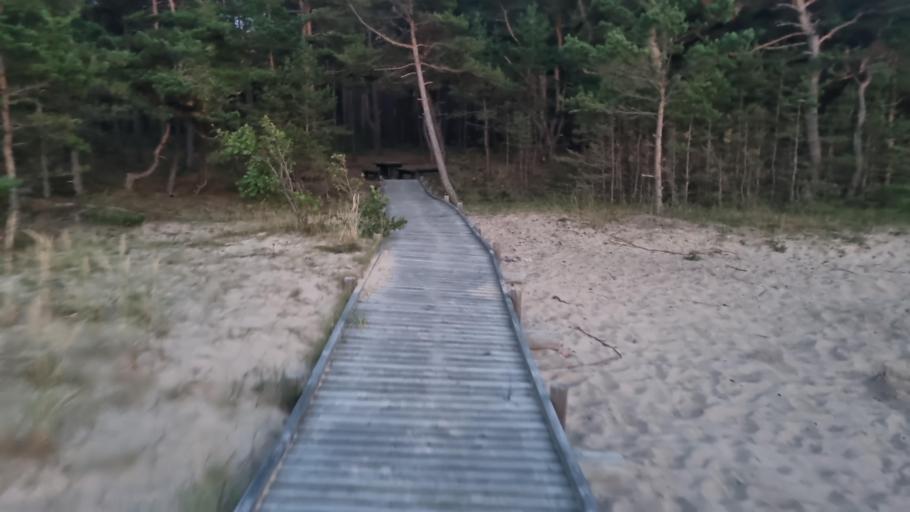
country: LV
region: Ventspils
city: Ventspils
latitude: 57.2480
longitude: 21.4145
